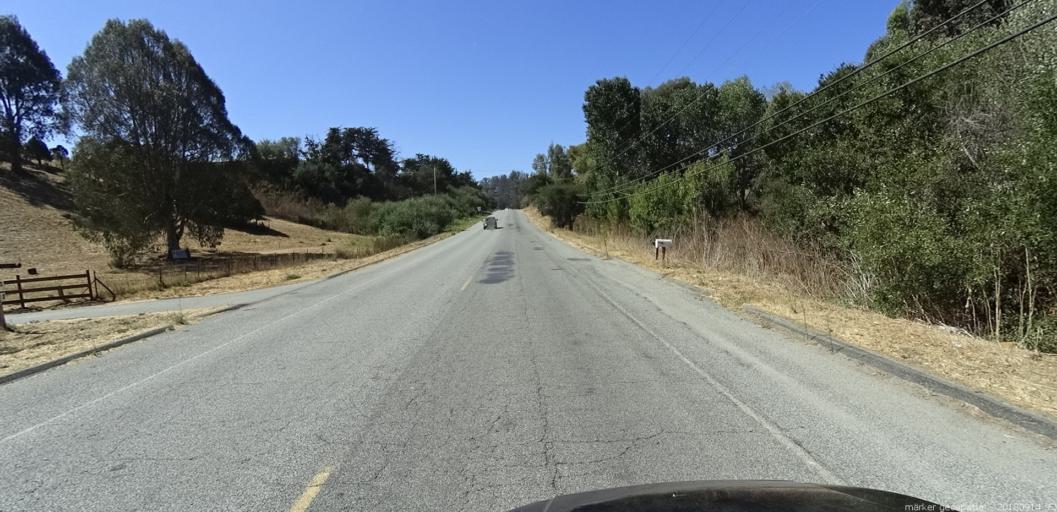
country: US
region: California
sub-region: San Benito County
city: Aromas
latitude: 36.8631
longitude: -121.6503
